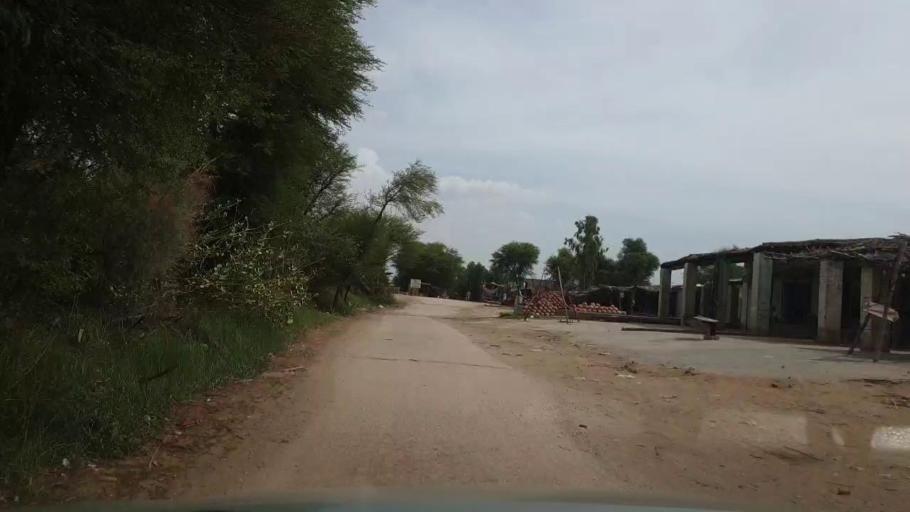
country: PK
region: Sindh
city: Kot Diji
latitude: 27.1361
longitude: 69.0280
